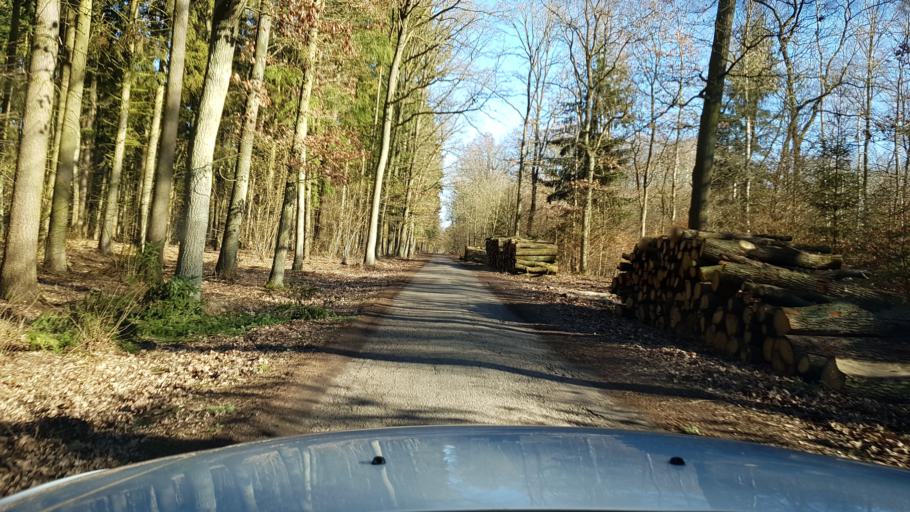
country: PL
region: West Pomeranian Voivodeship
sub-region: Powiat pyrzycki
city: Lipiany
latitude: 53.0327
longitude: 15.0273
